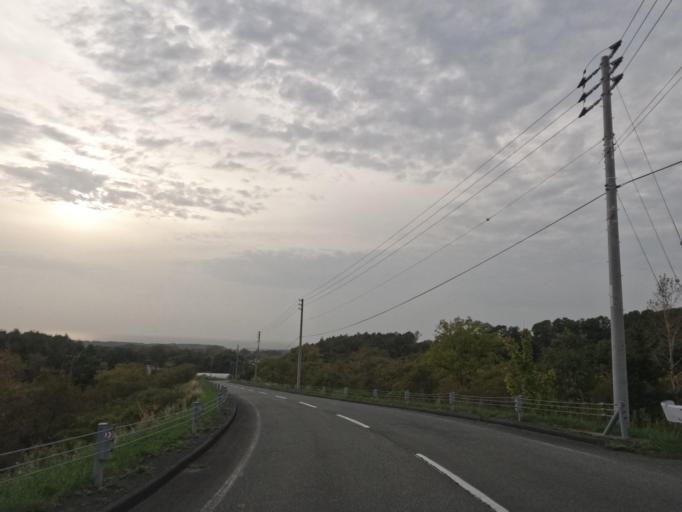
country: JP
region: Hokkaido
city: Date
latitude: 42.4174
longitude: 140.9246
